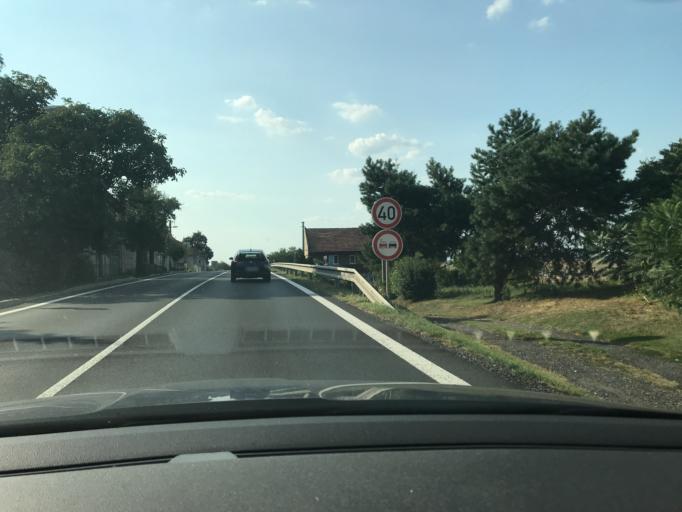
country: CZ
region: Central Bohemia
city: Klobuky
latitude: 50.2534
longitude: 14.0283
